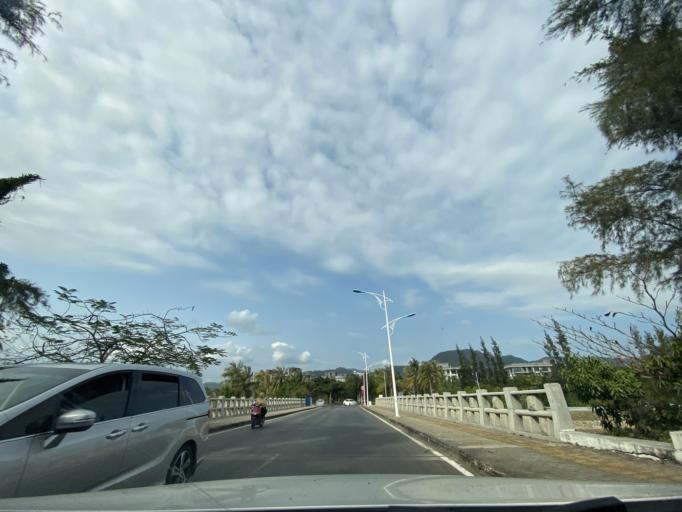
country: CN
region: Hainan
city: Tiandu
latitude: 18.2330
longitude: 109.6174
